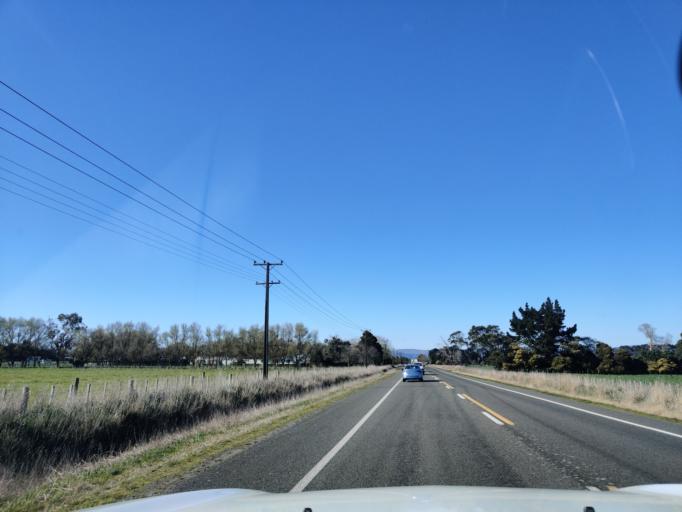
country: NZ
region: Manawatu-Wanganui
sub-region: Palmerston North City
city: Palmerston North
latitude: -40.3015
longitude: 175.5803
